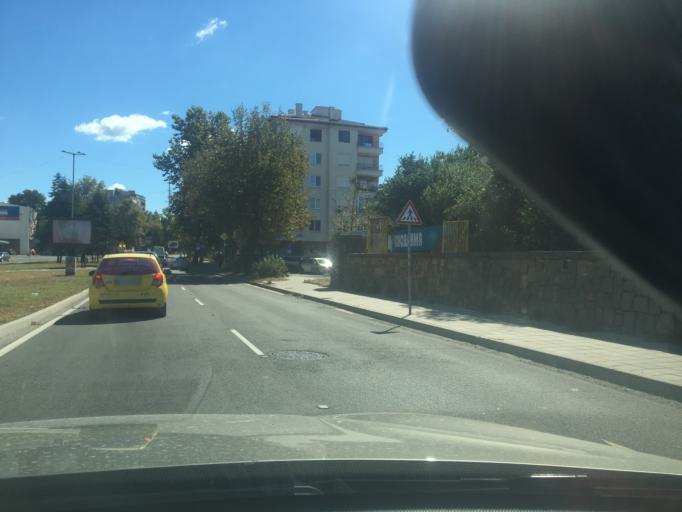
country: BG
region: Burgas
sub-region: Obshtina Burgas
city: Burgas
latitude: 42.5108
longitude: 27.4664
